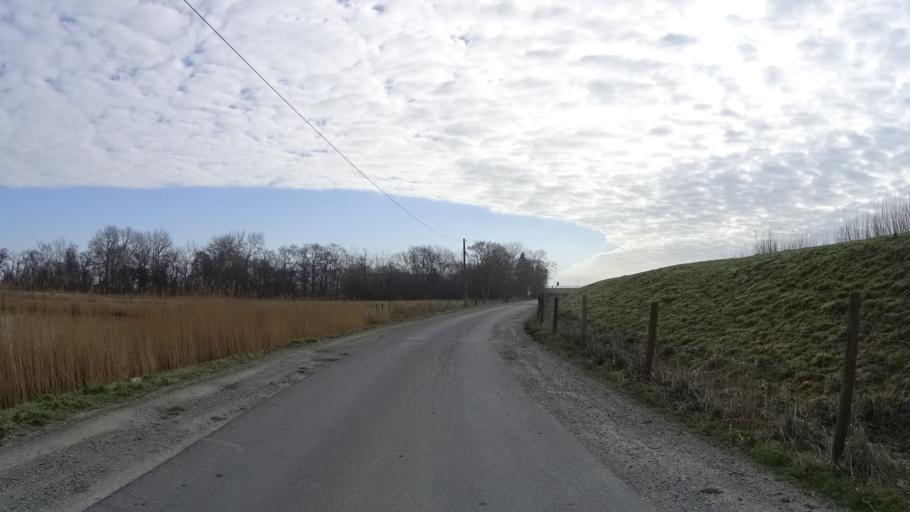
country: DE
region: Lower Saxony
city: Emden
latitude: 53.4028
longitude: 7.3205
